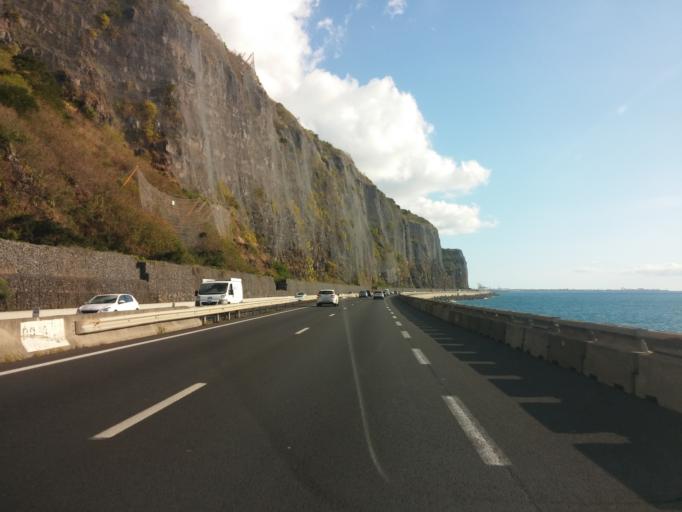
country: RE
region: Reunion
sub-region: Reunion
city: La Possession
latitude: -20.9062
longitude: 55.3628
